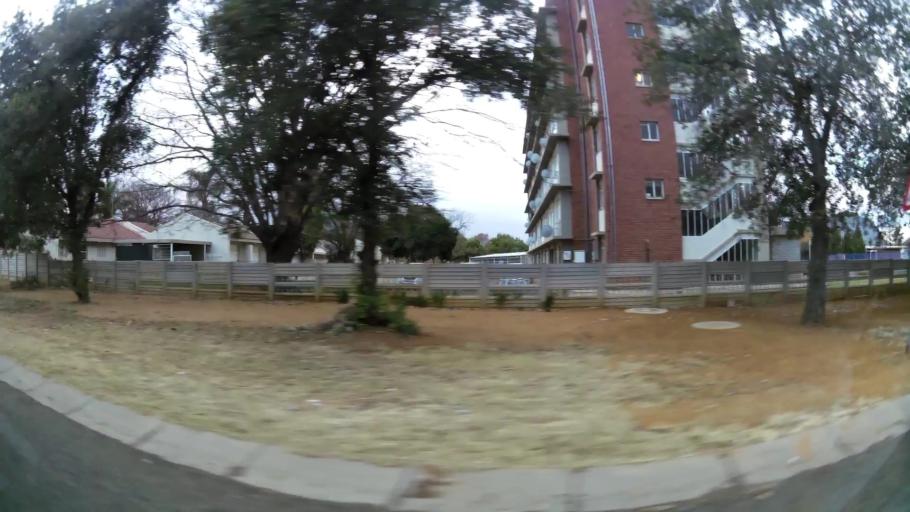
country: ZA
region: Orange Free State
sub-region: Lejweleputswa District Municipality
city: Welkom
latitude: -27.9622
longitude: 26.7387
